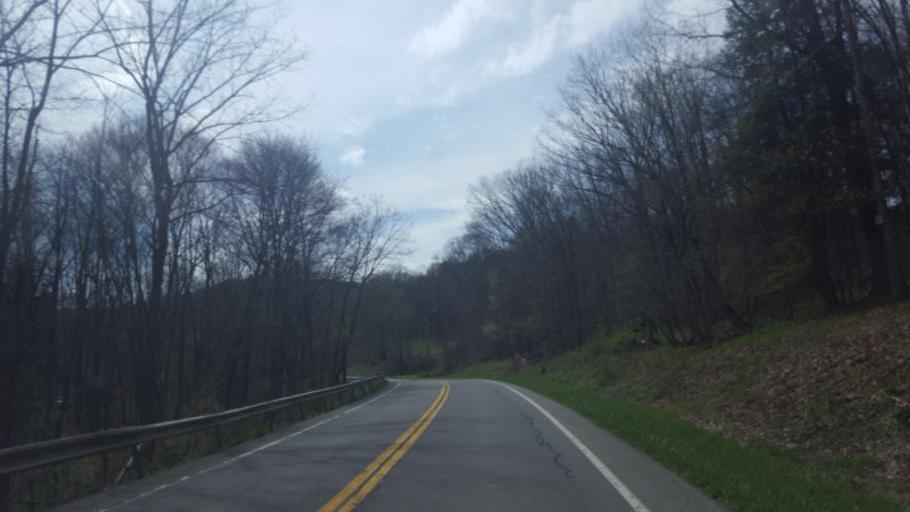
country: US
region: Pennsylvania
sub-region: Venango County
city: Sugarcreek
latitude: 41.3581
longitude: -79.9639
